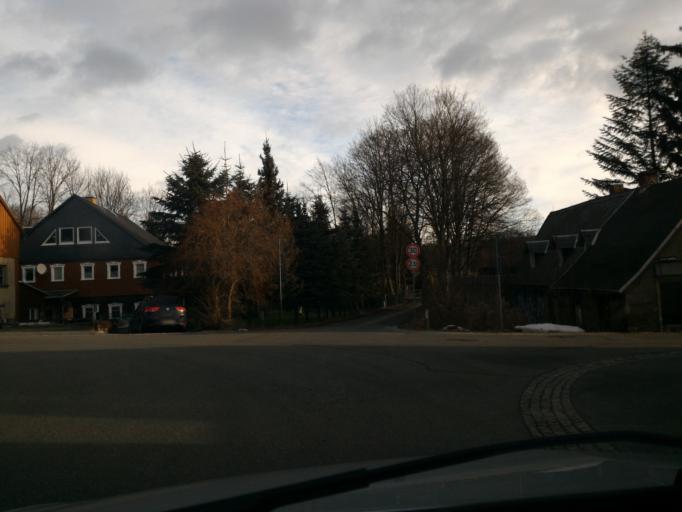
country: DE
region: Saxony
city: Oppach
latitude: 51.0612
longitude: 14.5037
